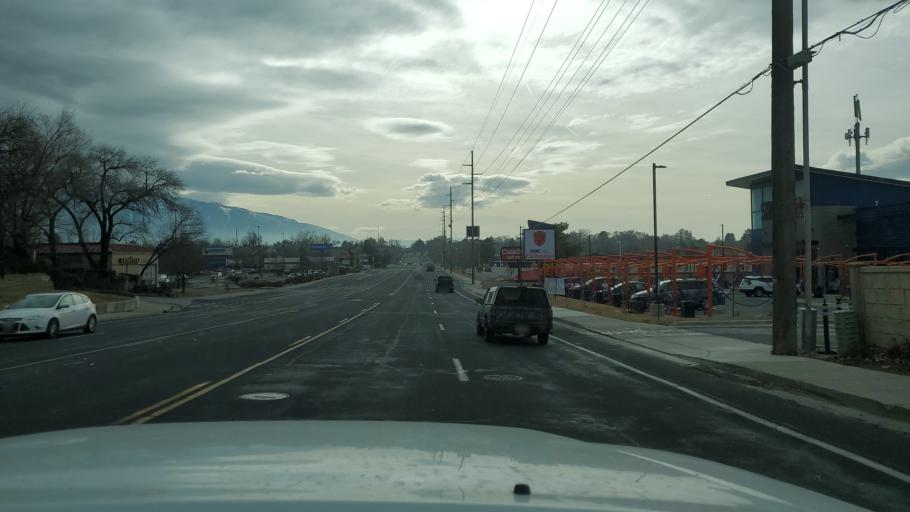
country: US
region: Utah
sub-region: Salt Lake County
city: Millcreek
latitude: 40.6707
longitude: -111.8655
